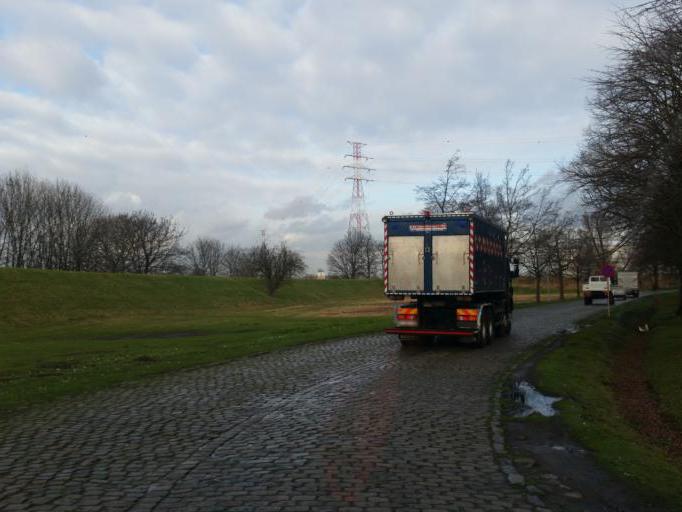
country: BE
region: Flanders
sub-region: Provincie Antwerpen
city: Stabroek
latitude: 51.3047
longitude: 4.2874
